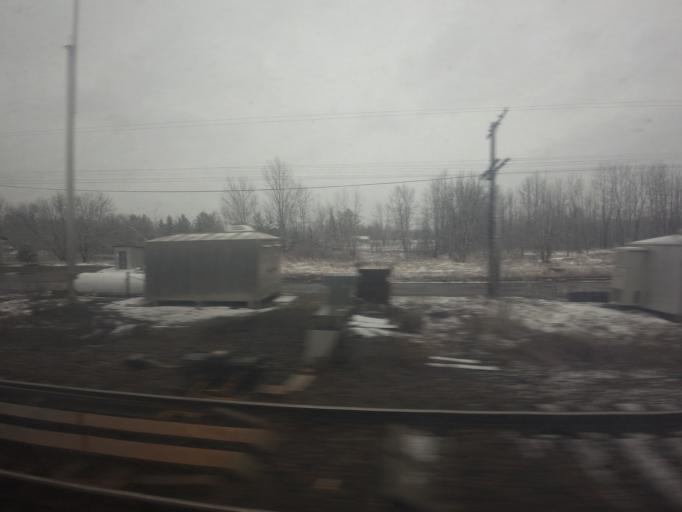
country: US
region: New York
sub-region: Jefferson County
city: Alexandria Bay
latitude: 44.4783
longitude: -75.8872
